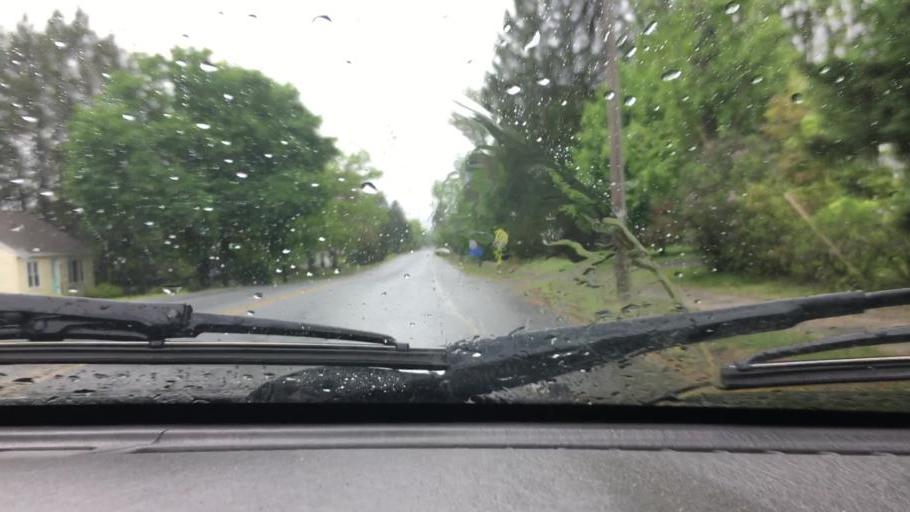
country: US
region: Massachusetts
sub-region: Franklin County
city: Turners Falls
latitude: 42.5890
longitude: -72.5388
